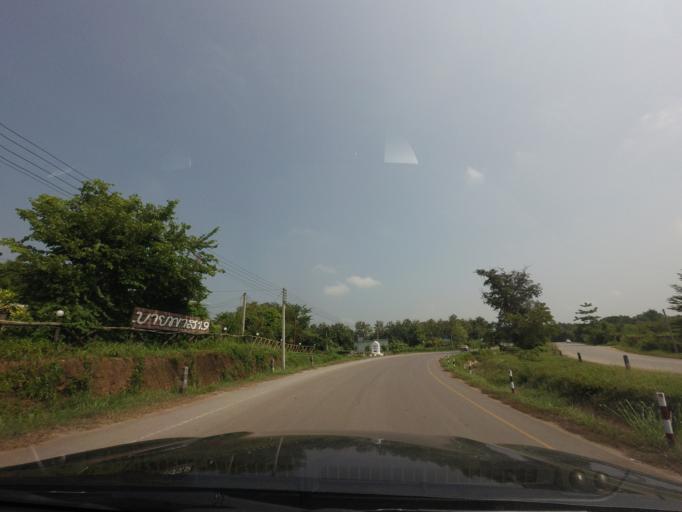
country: TH
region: Nan
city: Nan
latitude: 18.7957
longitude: 100.7557
